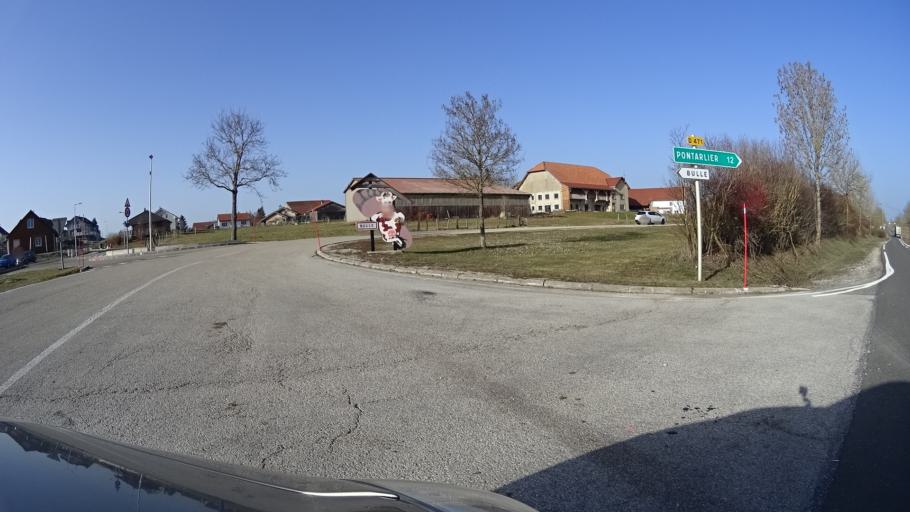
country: FR
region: Franche-Comte
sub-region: Departement du Doubs
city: Frasne
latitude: 46.8900
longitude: 6.2204
